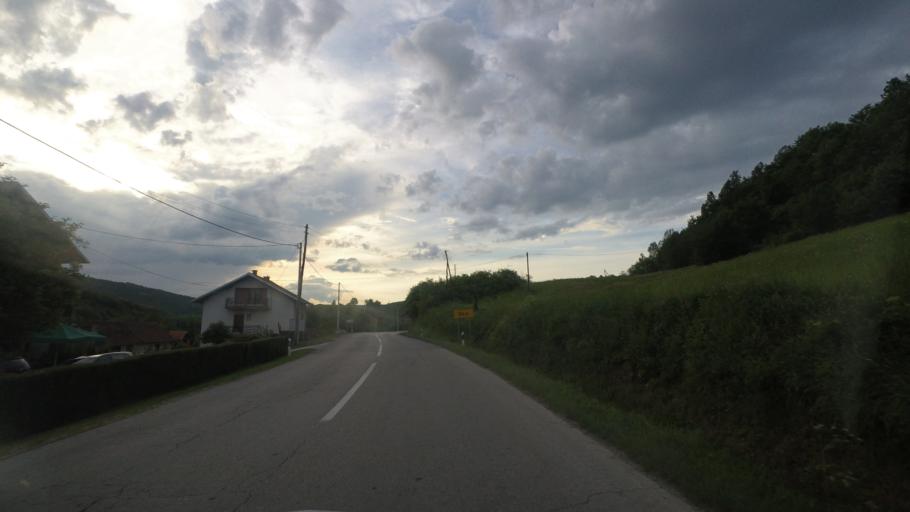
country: HR
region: Karlovacka
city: Vojnic
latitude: 45.3672
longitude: 15.6633
